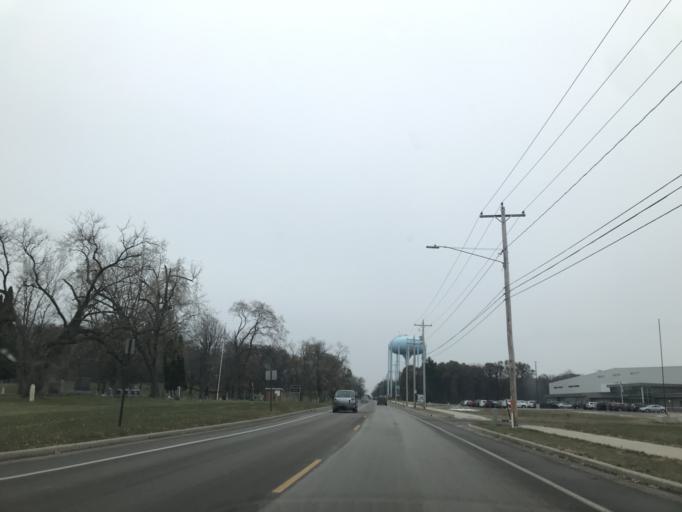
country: US
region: Wisconsin
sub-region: Marinette County
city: Marinette
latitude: 45.0815
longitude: -87.6296
